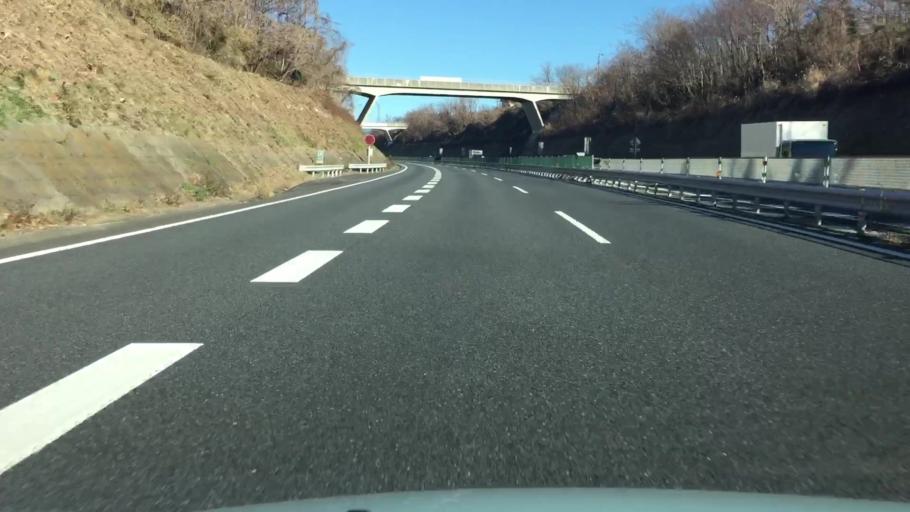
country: JP
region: Gunma
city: Shibukawa
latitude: 36.4860
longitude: 139.0286
